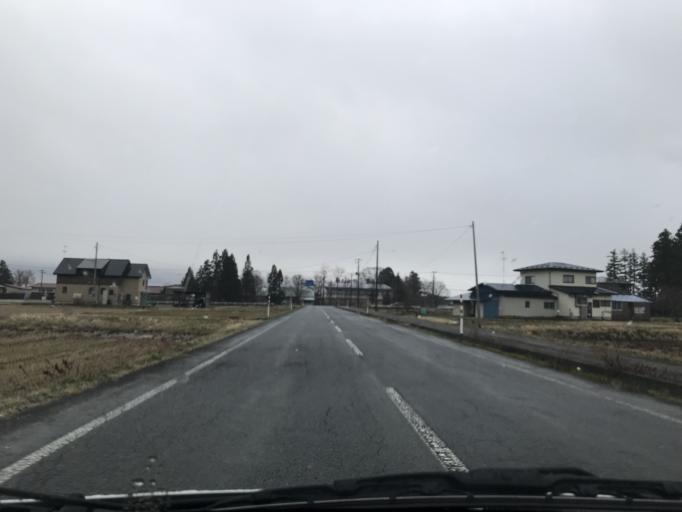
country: JP
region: Iwate
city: Mizusawa
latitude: 39.1979
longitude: 141.0899
